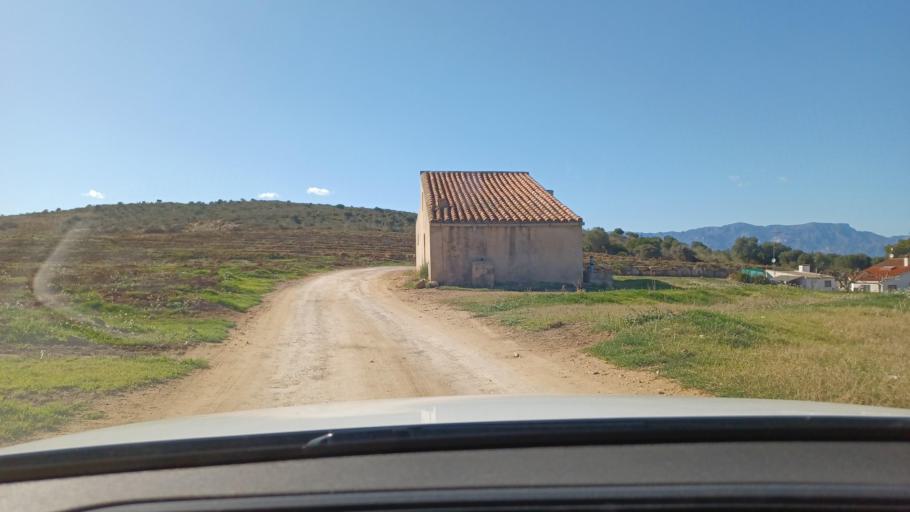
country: ES
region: Catalonia
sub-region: Provincia de Tarragona
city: Masdenverge
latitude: 40.6839
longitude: 0.5386
